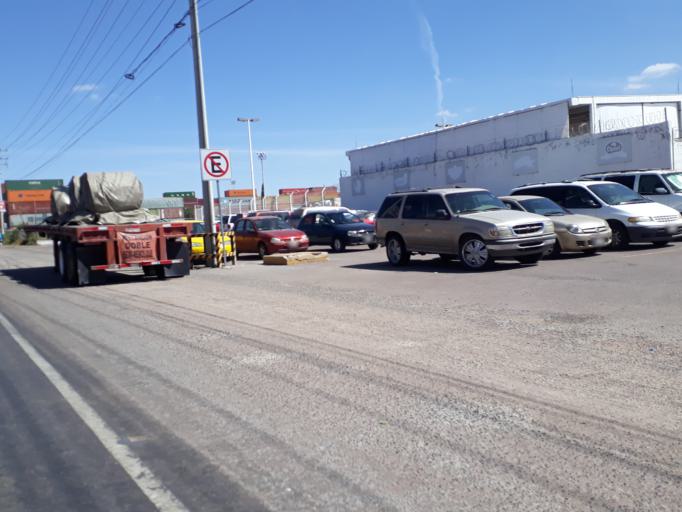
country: MX
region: Aguascalientes
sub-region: Aguascalientes
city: San Sebastian [Fraccionamiento]
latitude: 21.7980
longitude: -102.2798
